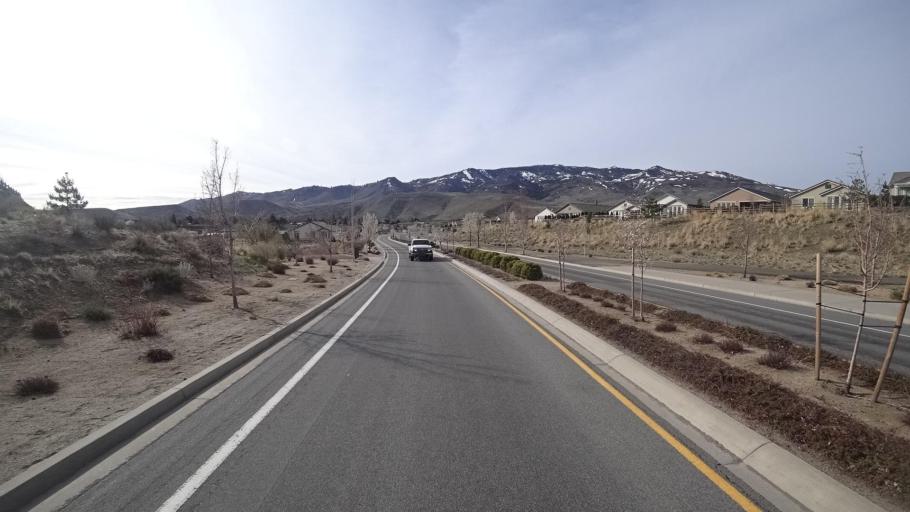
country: US
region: Nevada
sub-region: Washoe County
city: Mogul
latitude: 39.5158
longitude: -119.9424
